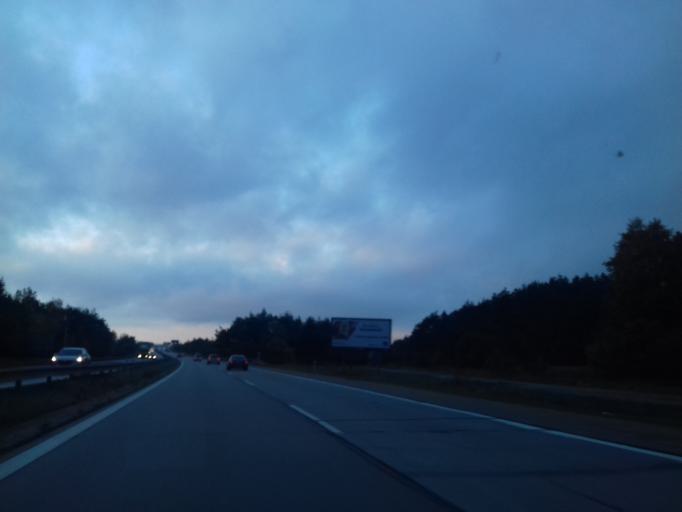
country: CZ
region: Vysocina
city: Krizanov
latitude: 49.3164
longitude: 16.1003
